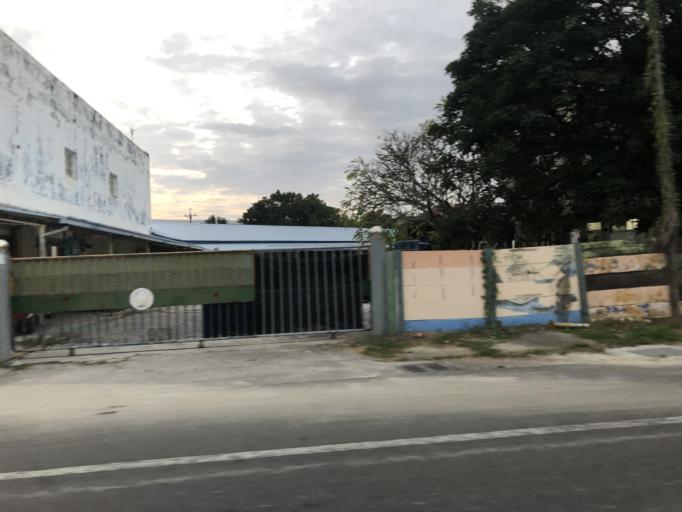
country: TW
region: Taiwan
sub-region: Tainan
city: Tainan
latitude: 23.0216
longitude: 120.2877
